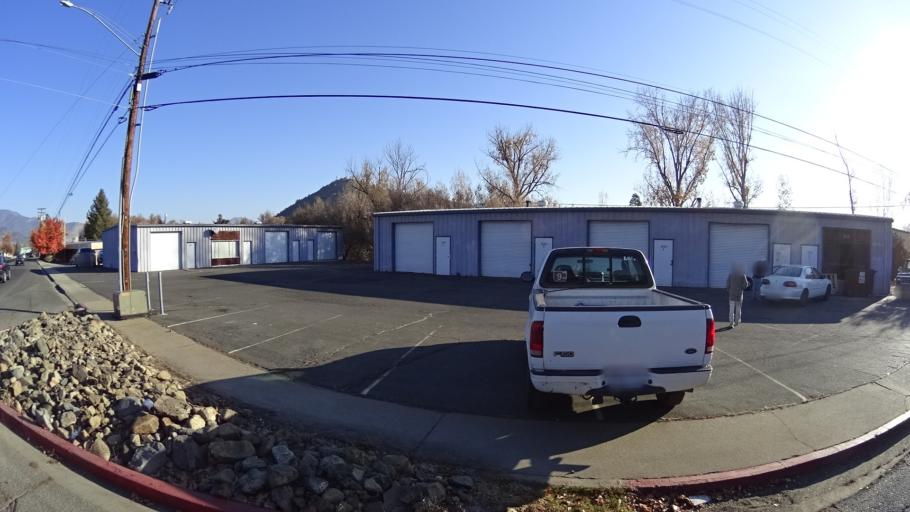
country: US
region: California
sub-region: Siskiyou County
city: Yreka
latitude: 41.7170
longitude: -122.6420
